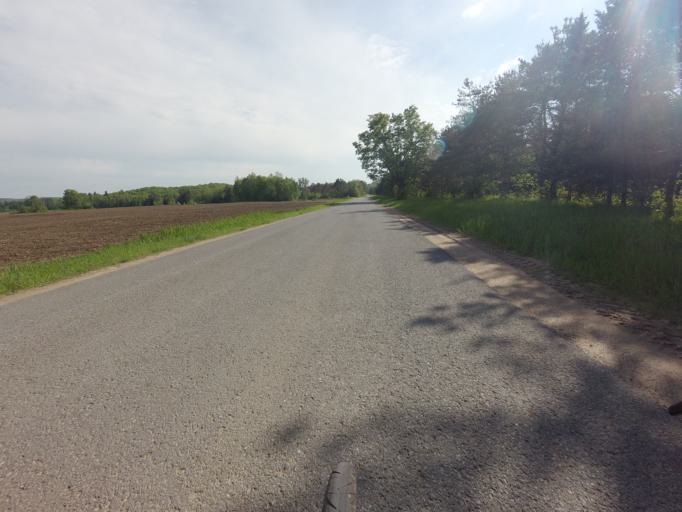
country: US
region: New York
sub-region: St. Lawrence County
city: Gouverneur
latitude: 44.2273
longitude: -75.2303
